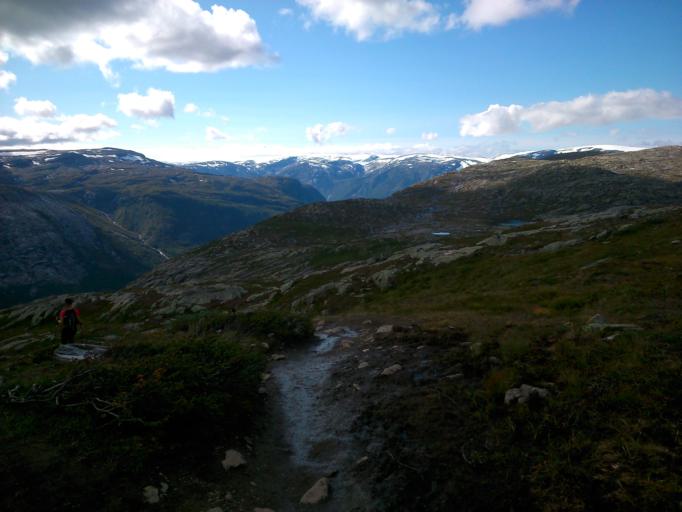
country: NO
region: Hordaland
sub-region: Odda
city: Odda
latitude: 60.1392
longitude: 6.7034
